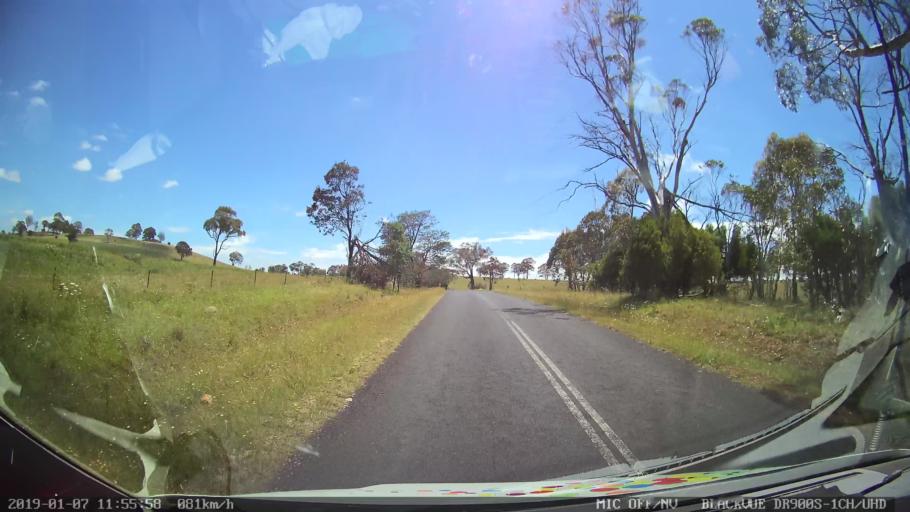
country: AU
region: New South Wales
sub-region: Guyra
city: Guyra
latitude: -30.2798
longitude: 151.6731
